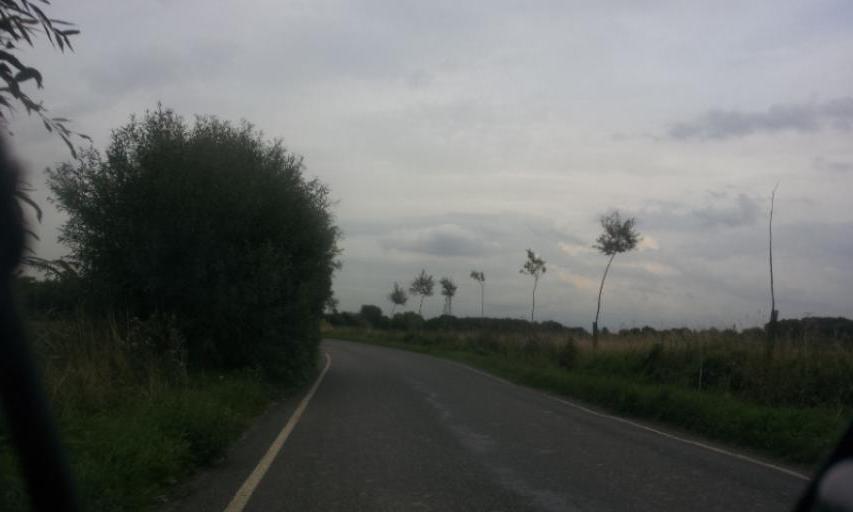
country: GB
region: England
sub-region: Kent
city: Hadlow
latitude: 51.1977
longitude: 0.3278
